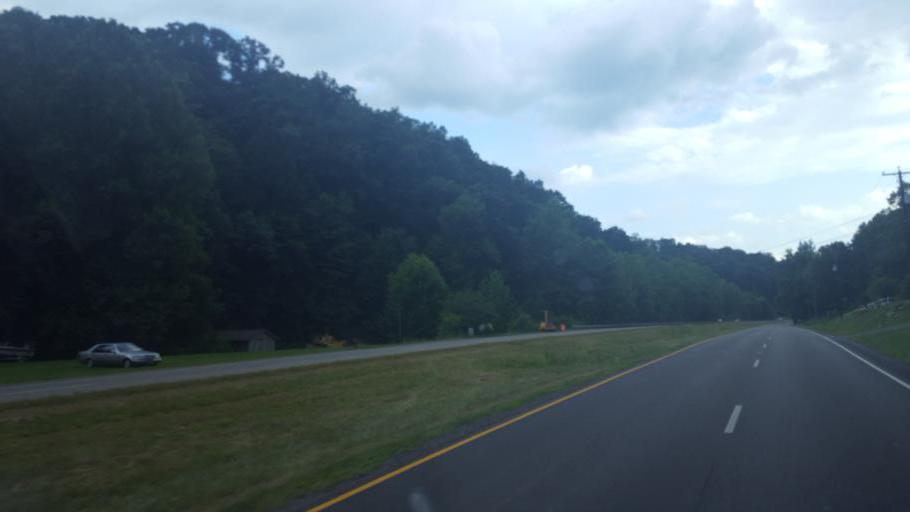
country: US
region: Virginia
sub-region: Wise County
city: Pound
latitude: 37.0773
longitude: -82.5989
